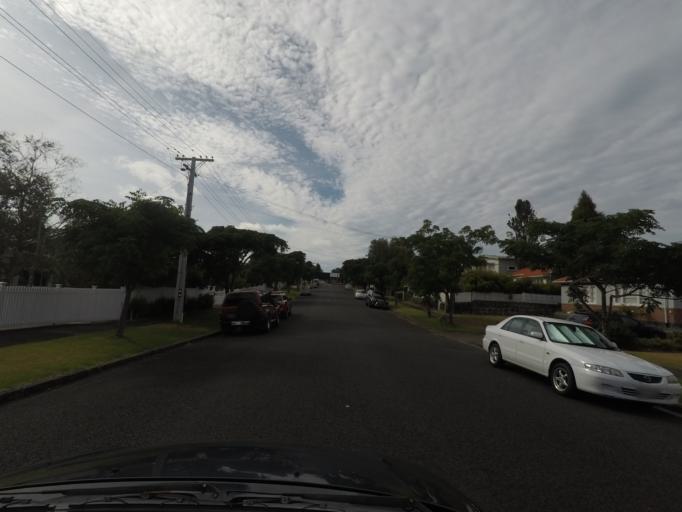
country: NZ
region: Auckland
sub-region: Auckland
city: Rosebank
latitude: -36.8753
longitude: 174.7181
